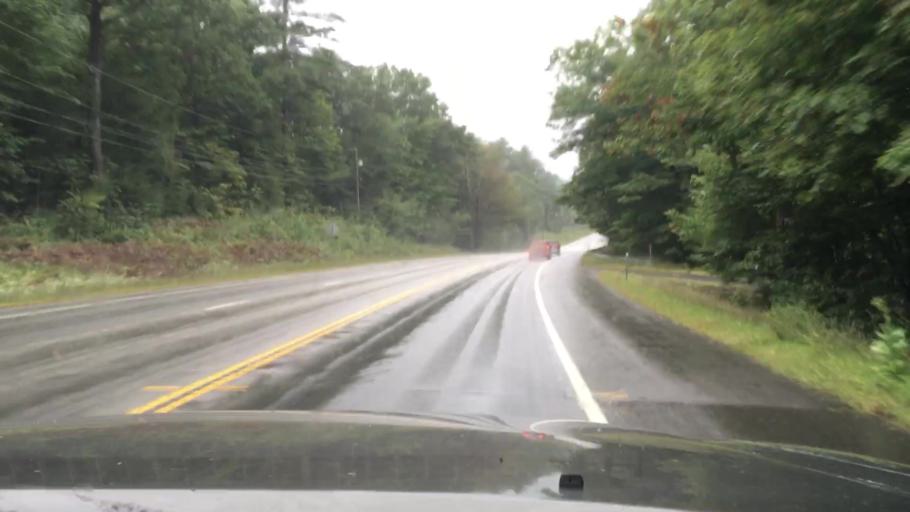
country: US
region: New Hampshire
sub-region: Cheshire County
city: West Swanzey
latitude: 42.9221
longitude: -72.3770
